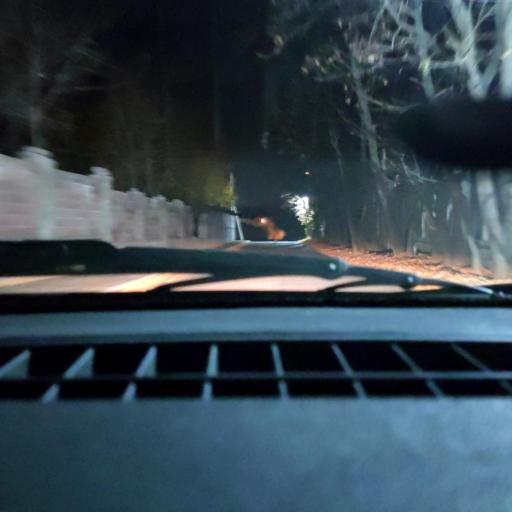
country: RU
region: Bashkortostan
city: Ufa
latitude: 54.7208
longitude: 56.0229
